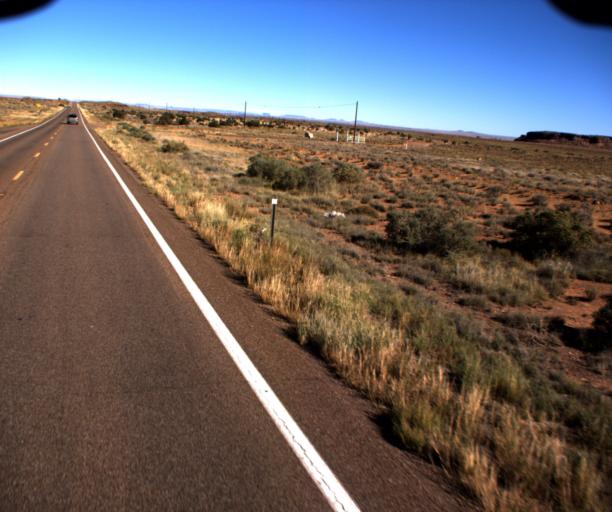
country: US
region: Arizona
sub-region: Navajo County
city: Holbrook
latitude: 34.8315
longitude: -110.1436
